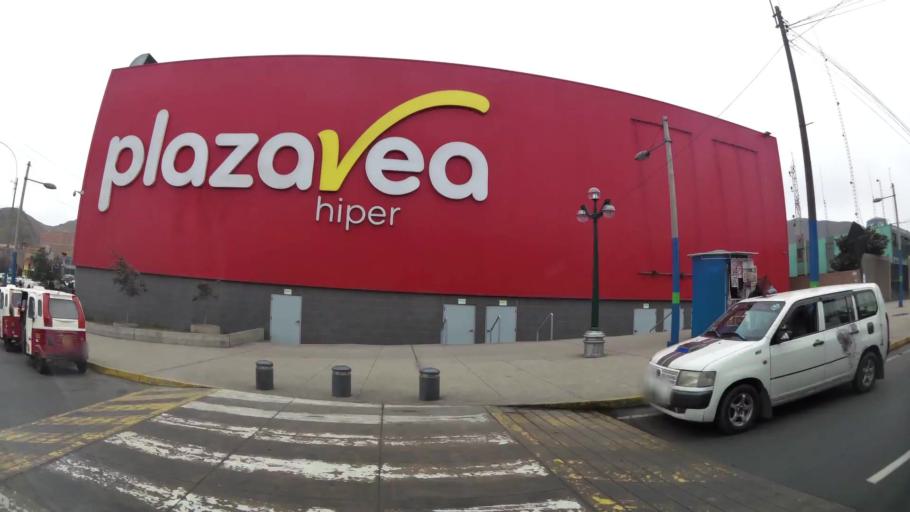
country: PE
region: Lima
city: Ventanilla
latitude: -11.8728
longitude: -77.1267
